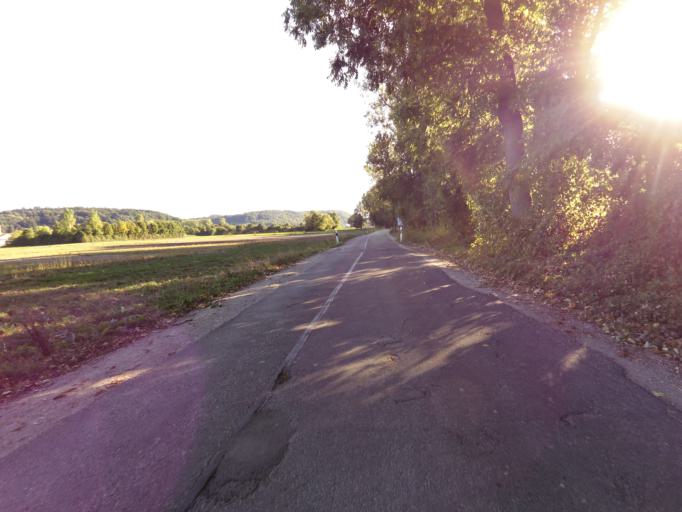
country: DE
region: Bavaria
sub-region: Lower Bavaria
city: Ergolding
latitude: 48.5619
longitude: 12.1947
